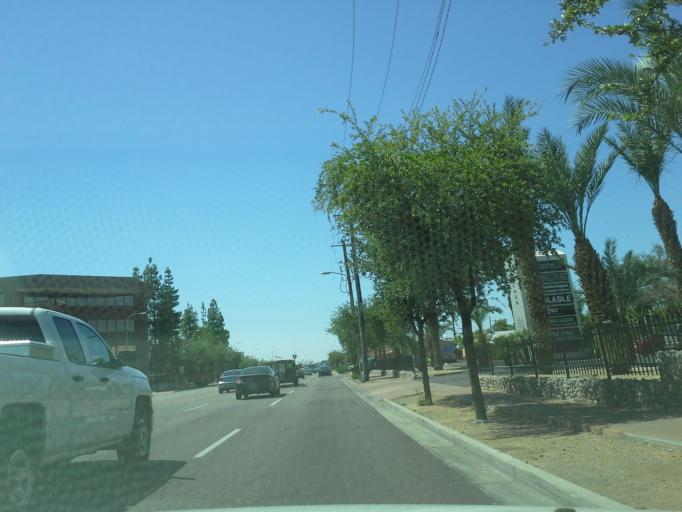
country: US
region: Arizona
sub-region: Maricopa County
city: Phoenix
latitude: 33.5097
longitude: -112.1014
